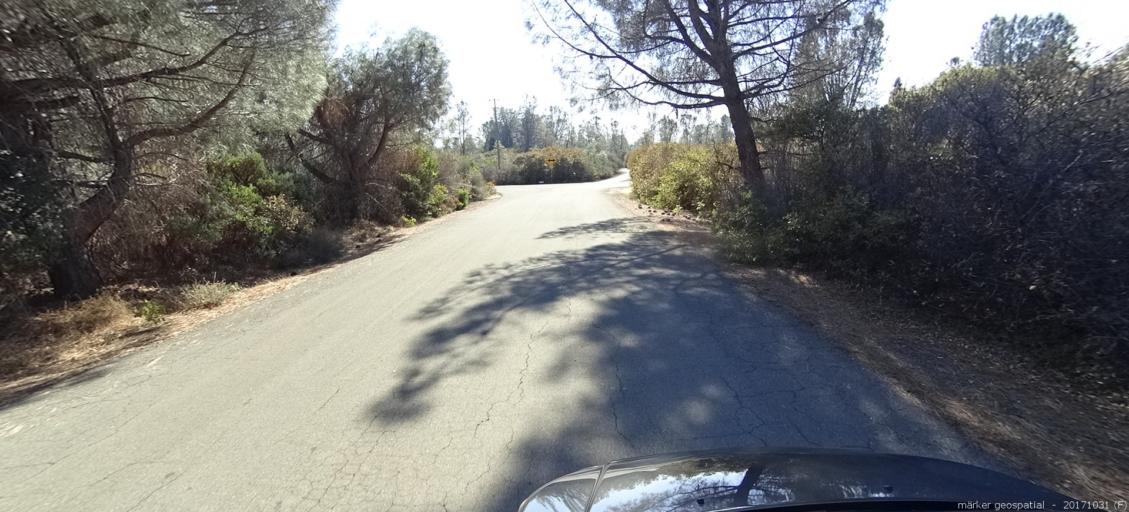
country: US
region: California
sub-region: Shasta County
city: Shingletown
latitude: 40.5094
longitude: -122.0244
